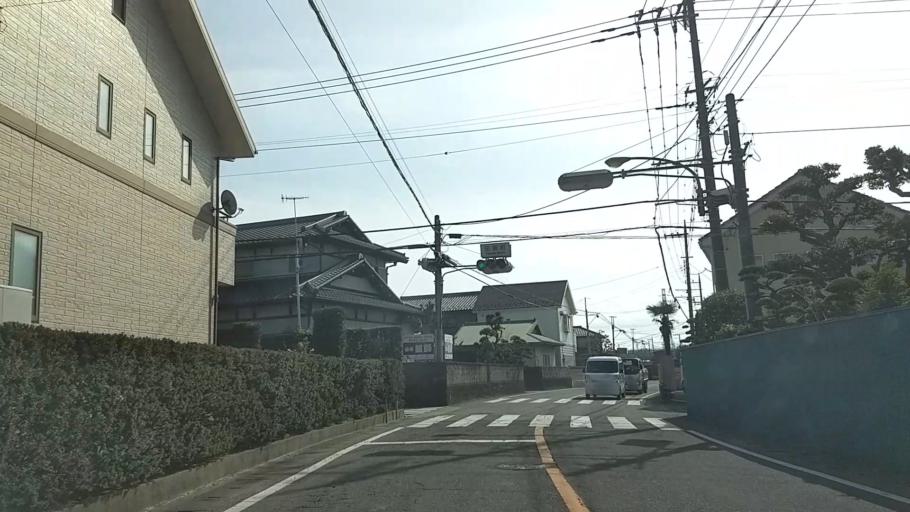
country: JP
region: Kanagawa
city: Chigasaki
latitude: 35.3551
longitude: 139.3848
